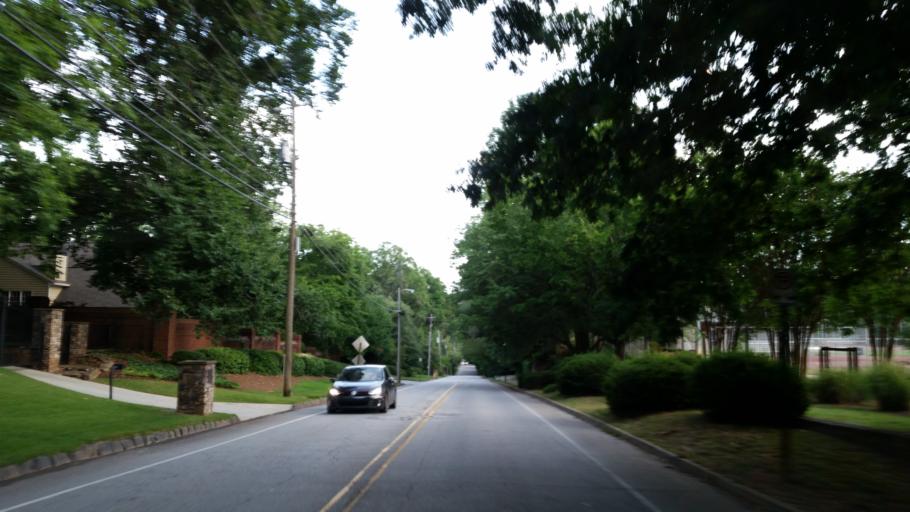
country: US
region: Georgia
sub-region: Fulton County
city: Sandy Springs
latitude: 33.8768
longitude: -84.3874
